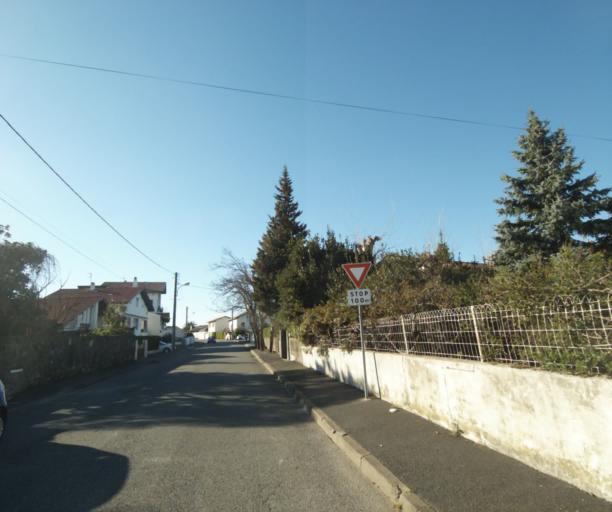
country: FR
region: Aquitaine
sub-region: Departement des Pyrenees-Atlantiques
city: Hendaye
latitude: 43.3624
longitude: -1.7572
